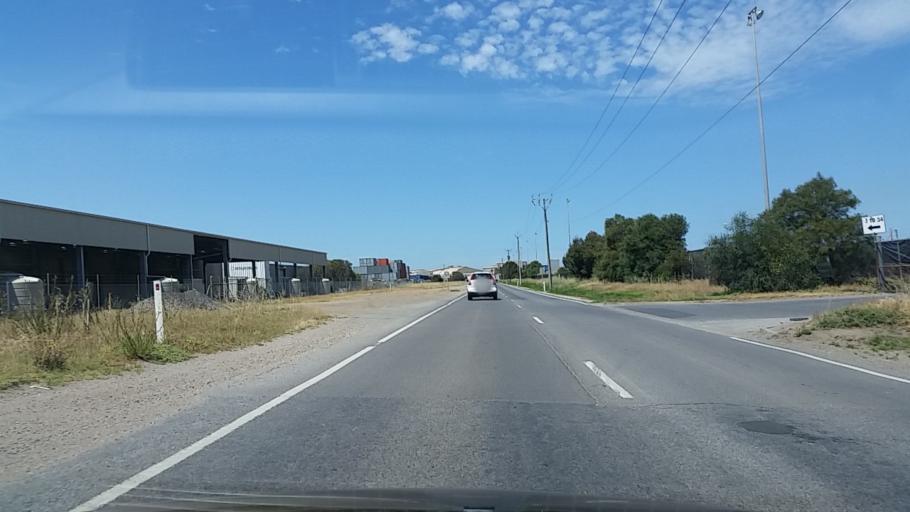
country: AU
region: South Australia
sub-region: Port Adelaide Enfield
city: Birkenhead
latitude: -34.8282
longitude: 138.5190
